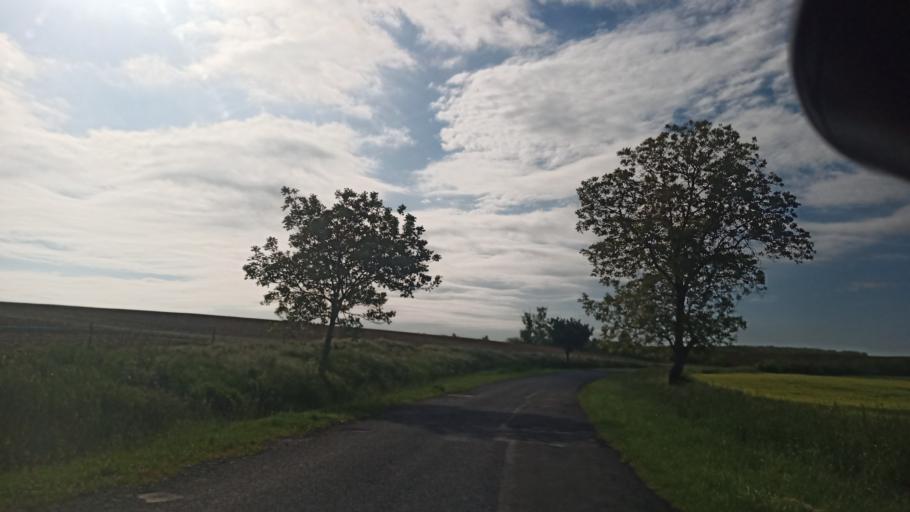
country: HU
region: Zala
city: Pacsa
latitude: 46.7052
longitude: 17.0514
